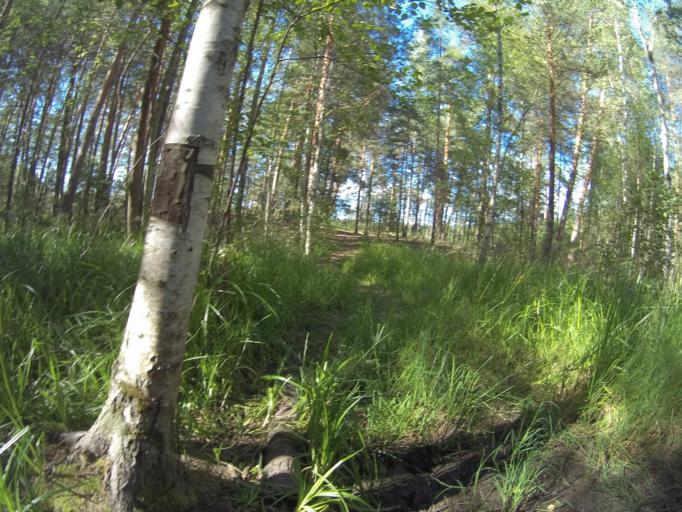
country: RU
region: Vladimir
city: Raduzhnyy
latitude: 56.0539
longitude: 40.3528
